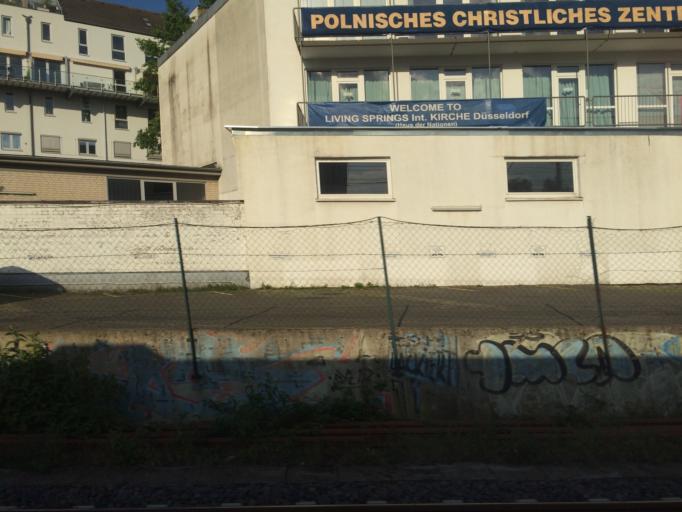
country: DE
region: North Rhine-Westphalia
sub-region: Regierungsbezirk Dusseldorf
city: Dusseldorf
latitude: 51.2313
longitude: 6.7976
